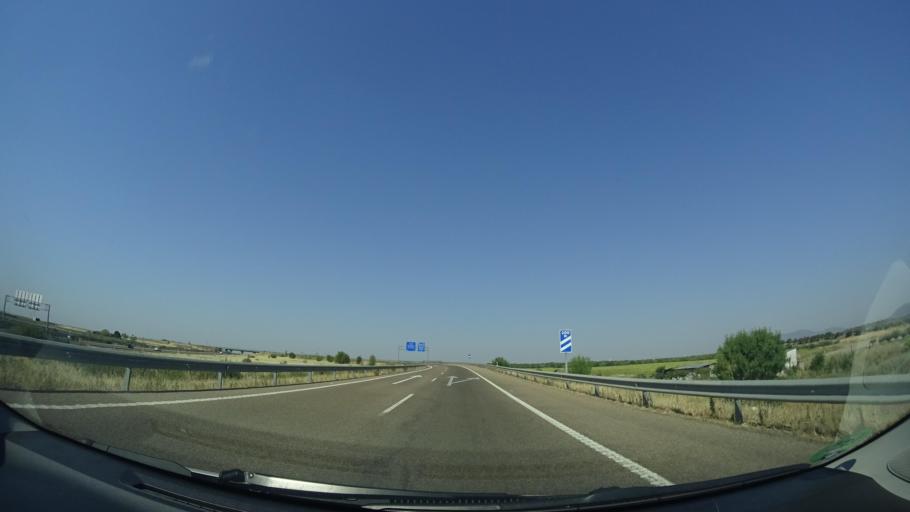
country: ES
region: Extremadura
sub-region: Provincia de Caceres
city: Miajadas
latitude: 39.1296
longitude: -5.9523
